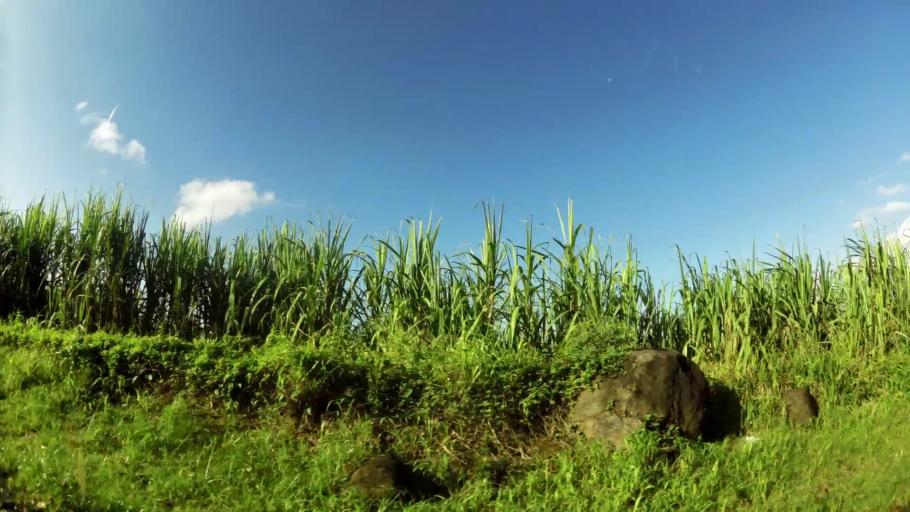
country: MQ
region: Martinique
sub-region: Martinique
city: Le Lamentin
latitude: 14.6315
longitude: -61.0314
